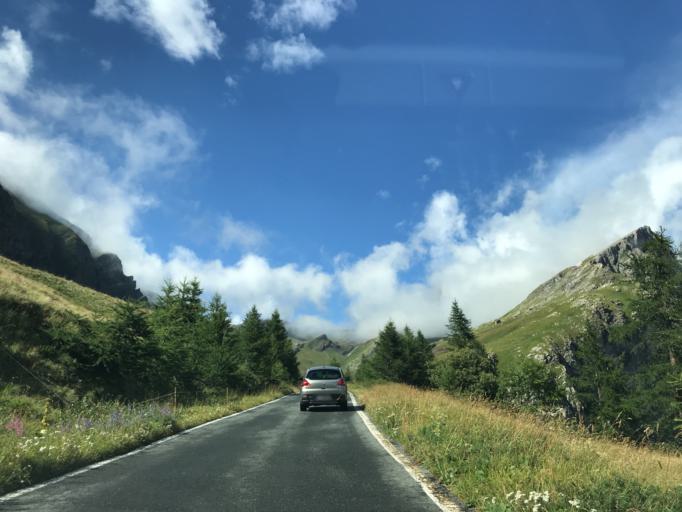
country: IT
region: Piedmont
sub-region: Provincia di Cuneo
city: Pontechianale
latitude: 44.6587
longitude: 6.9861
